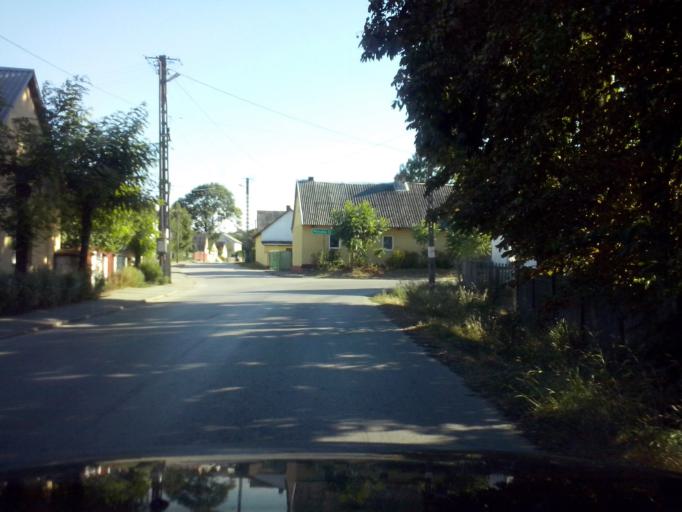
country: PL
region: Swietokrzyskie
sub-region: Powiat kielecki
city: Chmielnik
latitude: 50.5817
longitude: 20.7072
